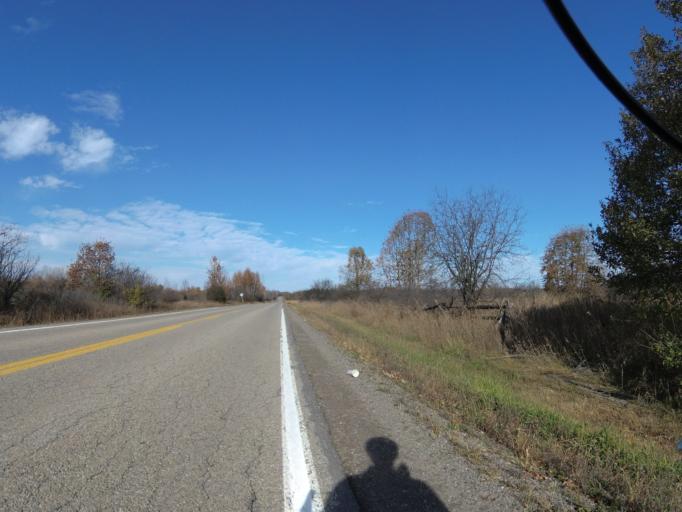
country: CA
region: Ontario
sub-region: Lanark County
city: Smiths Falls
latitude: 44.8286
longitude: -75.9386
